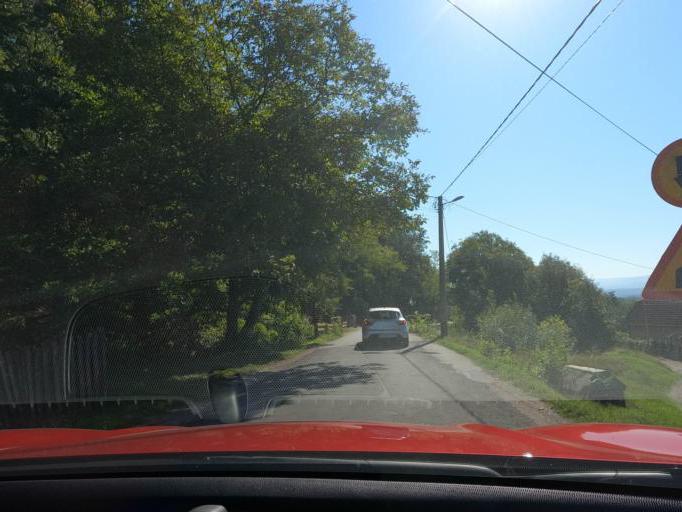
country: RS
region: Central Serbia
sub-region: Raski Okrug
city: Kraljevo
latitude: 43.7372
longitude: 20.7391
